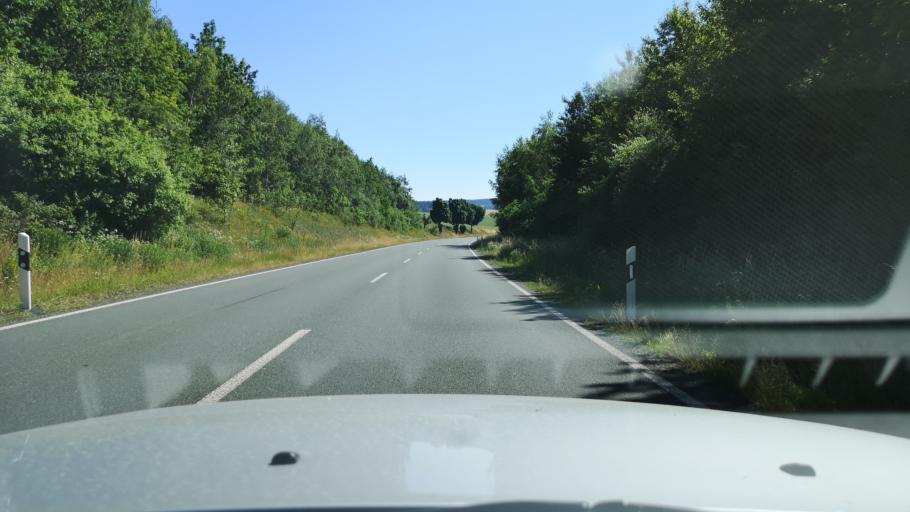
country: DE
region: Thuringia
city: Birkenhugel
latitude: 50.4457
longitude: 11.7845
